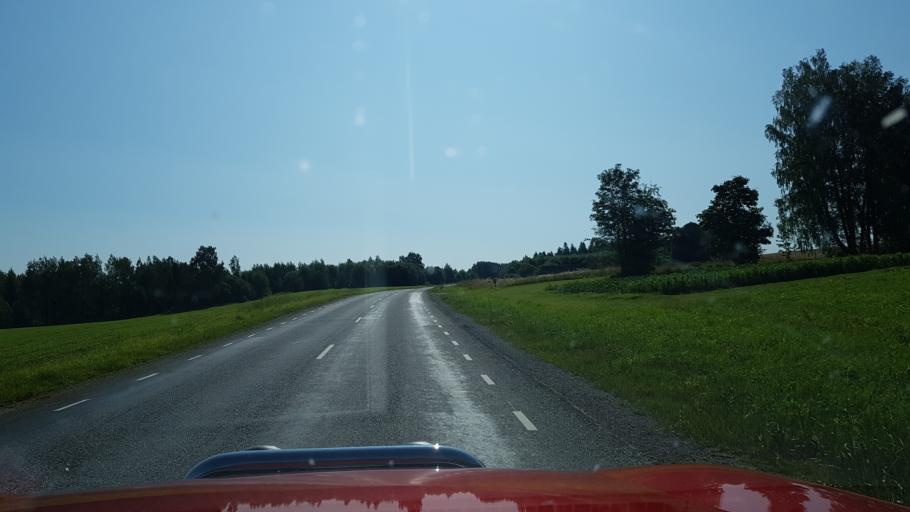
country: EE
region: Vorumaa
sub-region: Voru linn
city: Voru
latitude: 57.9762
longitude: 26.8199
